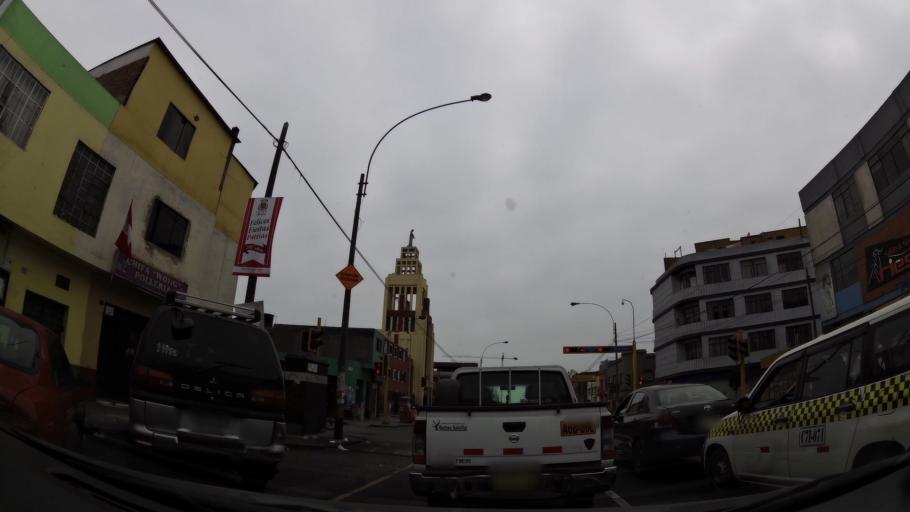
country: PE
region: Lima
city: Lima
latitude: -12.0552
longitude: -77.0507
